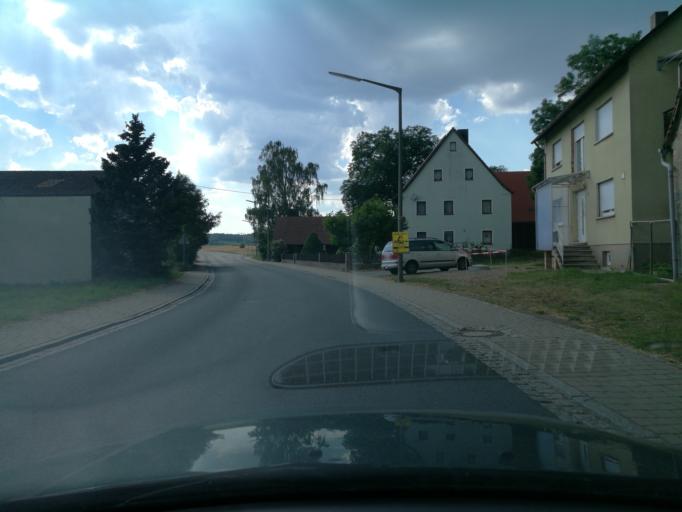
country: DE
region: Bavaria
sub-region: Regierungsbezirk Mittelfranken
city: Dietenhofen
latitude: 49.4198
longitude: 10.7354
